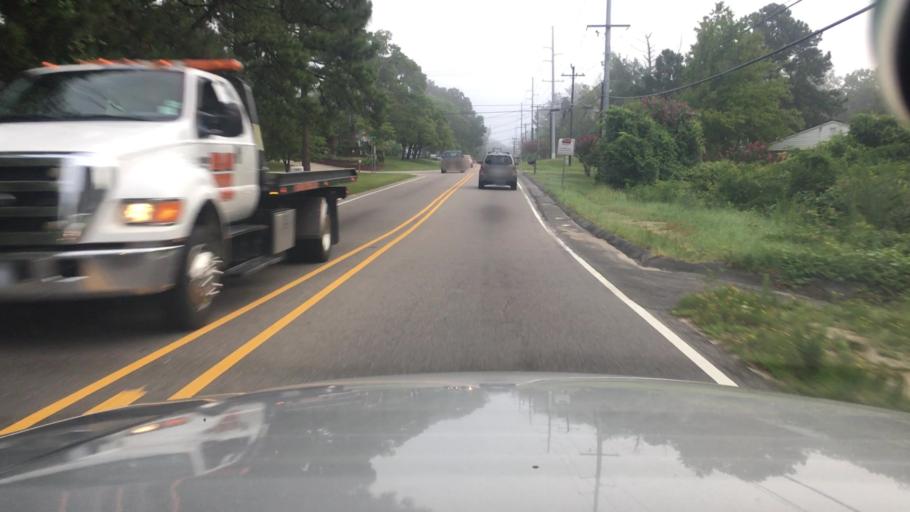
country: US
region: North Carolina
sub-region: Cumberland County
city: Hope Mills
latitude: 35.0167
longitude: -78.9401
